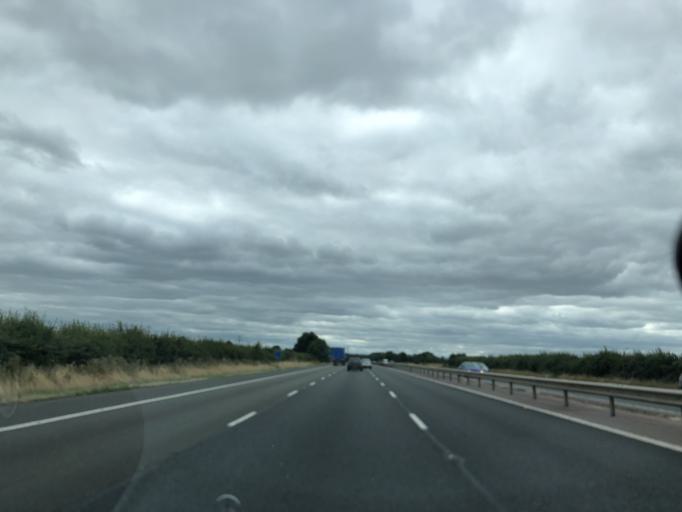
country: GB
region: England
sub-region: Oxfordshire
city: Wheatley
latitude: 51.7716
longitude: -1.1008
